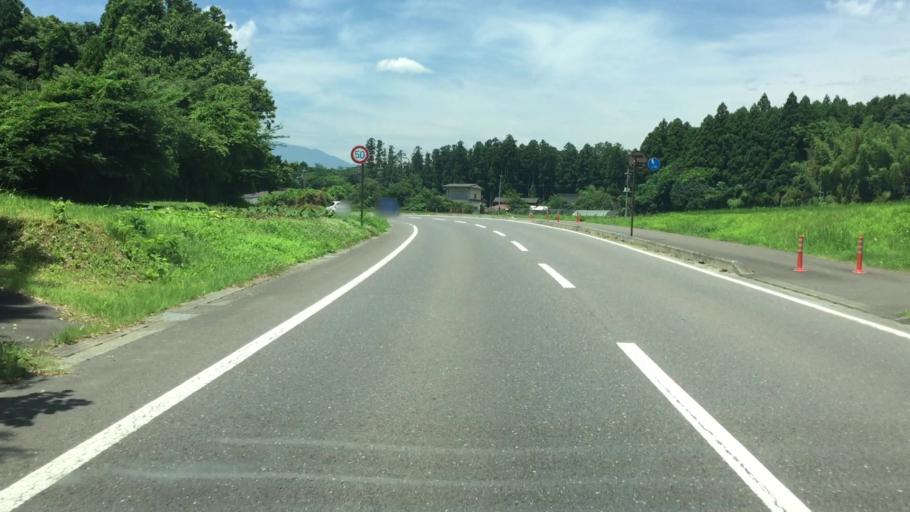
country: JP
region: Tochigi
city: Kuroiso
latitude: 37.0260
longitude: 140.0275
